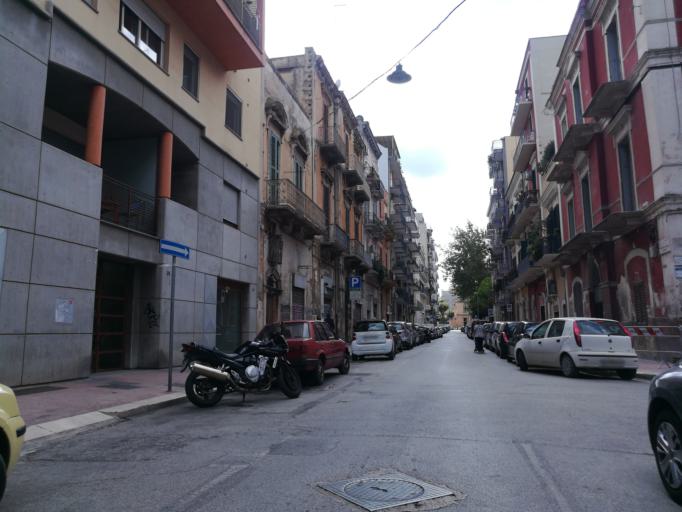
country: IT
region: Apulia
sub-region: Provincia di Bari
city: Bari
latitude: 41.1212
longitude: 16.8761
